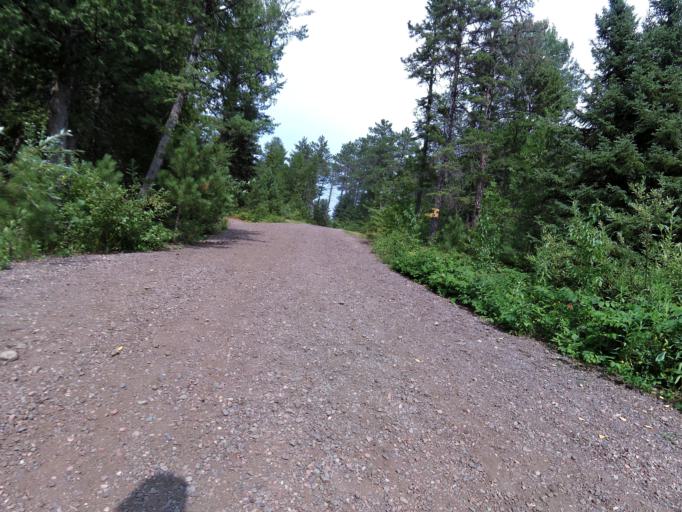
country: CA
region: Ontario
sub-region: Thunder Bay District
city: Thunder Bay
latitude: 48.7981
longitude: -88.6179
